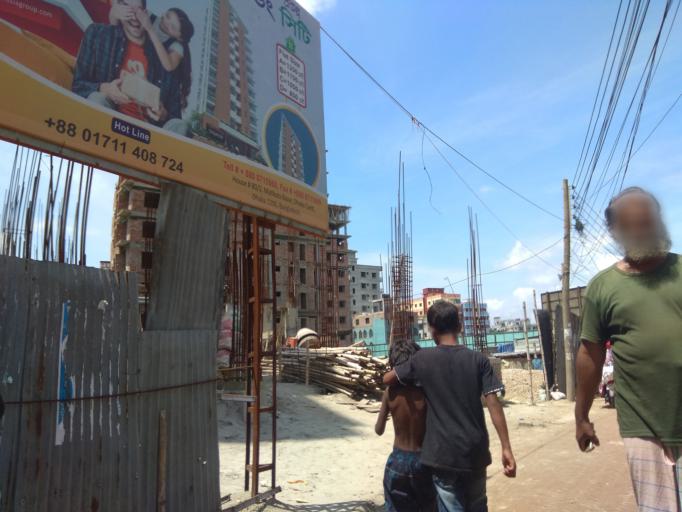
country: BD
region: Dhaka
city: Tungi
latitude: 23.8203
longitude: 90.3920
